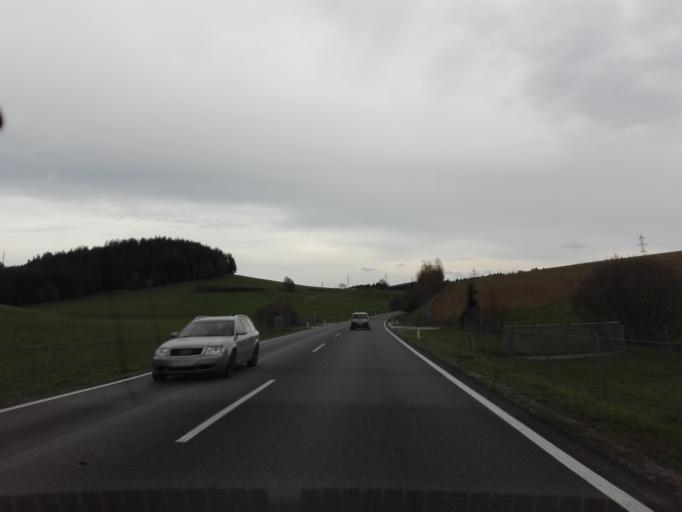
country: AT
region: Upper Austria
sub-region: Politischer Bezirk Rohrbach
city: Schlaegl
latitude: 48.5914
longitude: 13.9661
